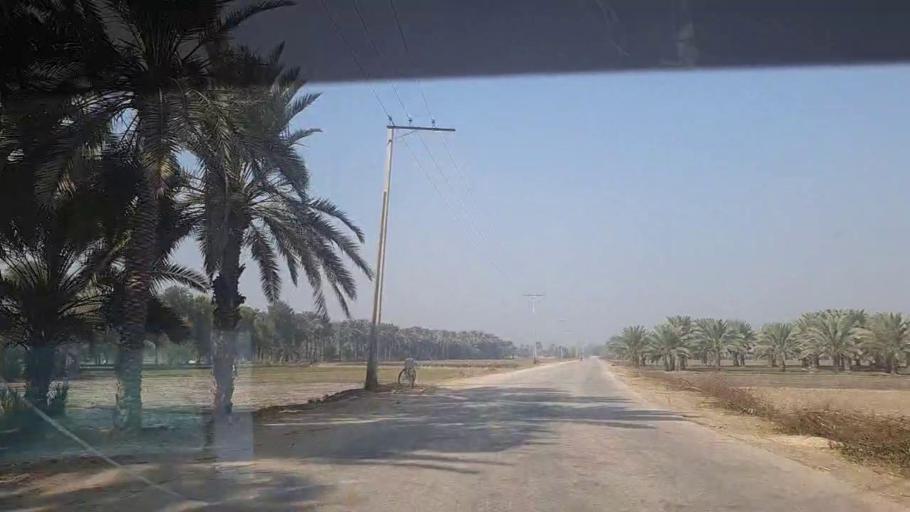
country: PK
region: Sindh
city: Kot Diji
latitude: 27.3666
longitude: 68.7025
